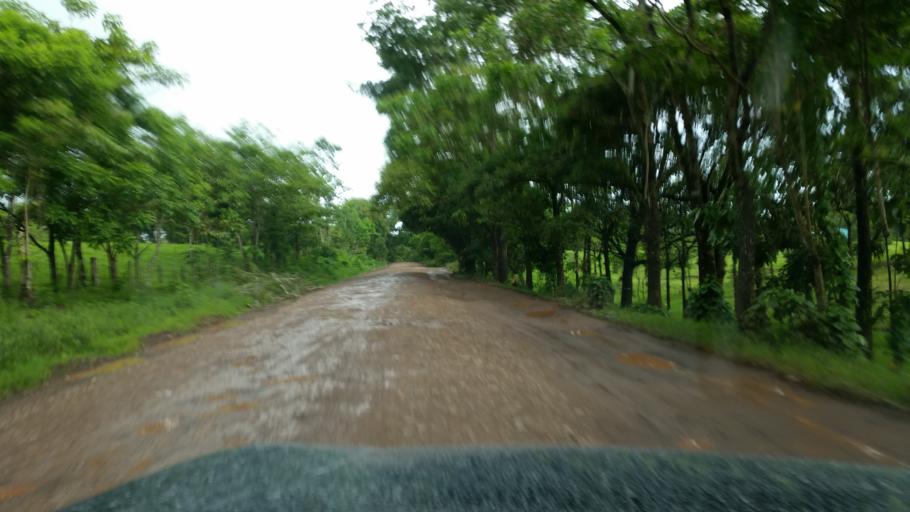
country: NI
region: Atlantico Norte (RAAN)
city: Siuna
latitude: 13.4142
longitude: -84.8535
